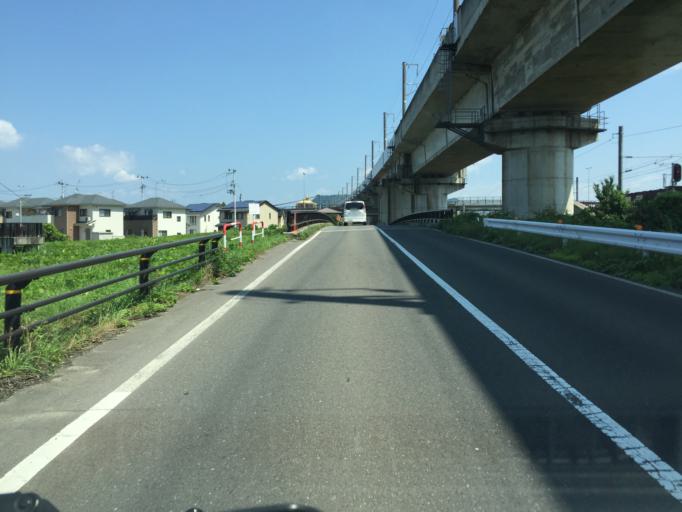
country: JP
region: Fukushima
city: Fukushima-shi
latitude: 37.7379
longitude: 140.4582
